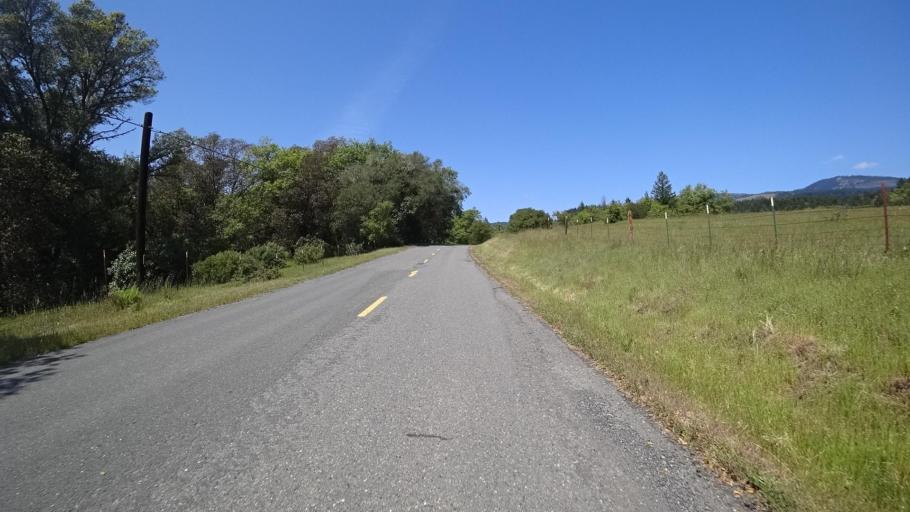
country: US
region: California
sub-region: Humboldt County
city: Redway
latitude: 40.2454
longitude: -123.6254
